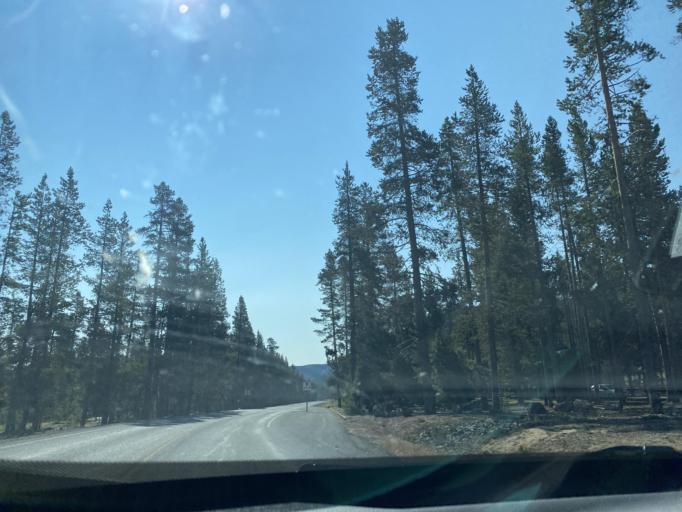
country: US
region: Oregon
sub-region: Deschutes County
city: Three Rivers
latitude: 43.7123
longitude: -121.2776
